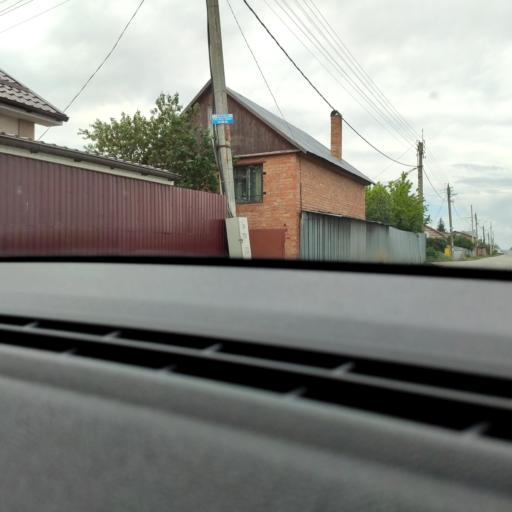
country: RU
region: Samara
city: Podstepki
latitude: 53.5073
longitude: 49.1611
